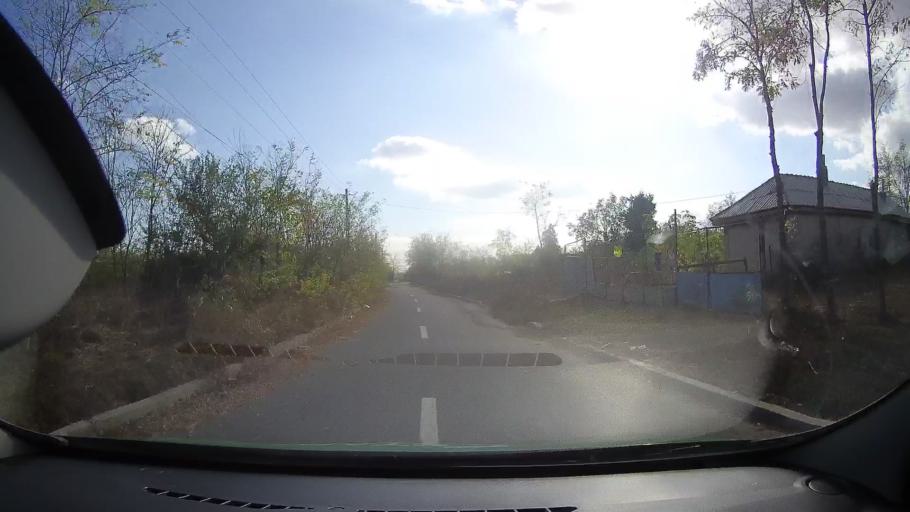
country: RO
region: Constanta
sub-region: Comuna Istria
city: Istria
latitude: 44.5771
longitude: 28.7122
